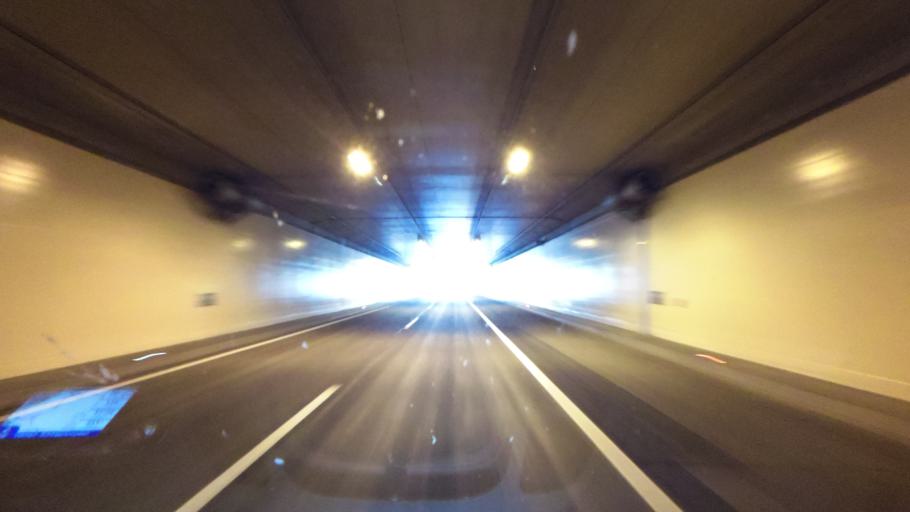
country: AT
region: Carinthia
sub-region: Politischer Bezirk Spittal an der Drau
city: Trebesing
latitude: 46.8848
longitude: 13.5134
